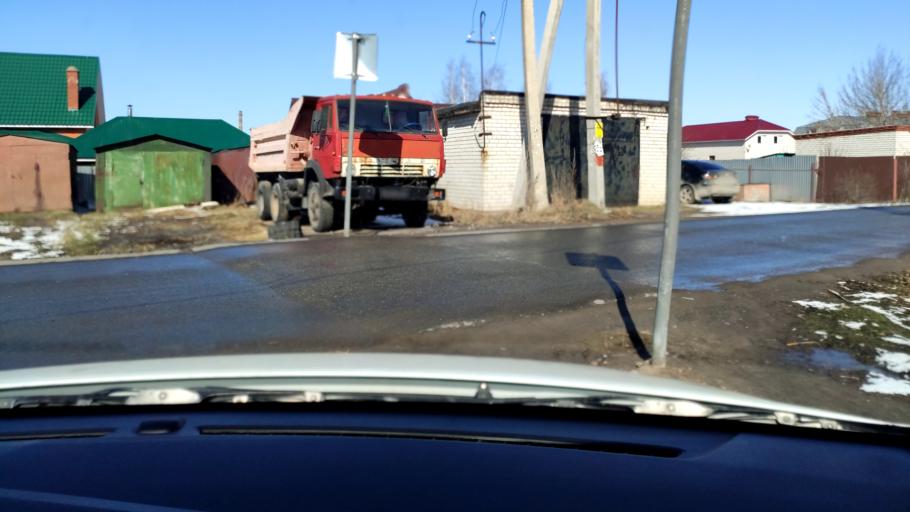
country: RU
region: Tatarstan
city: Vysokaya Gora
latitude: 55.8760
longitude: 49.2461
